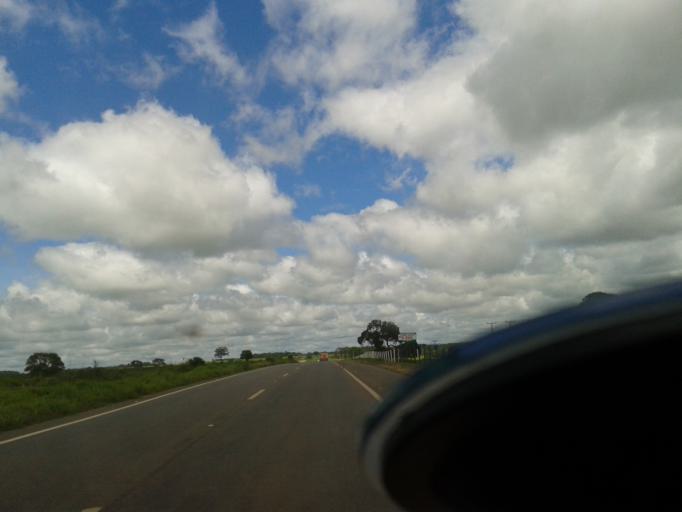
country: BR
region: Goias
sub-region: Itaberai
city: Itaberai
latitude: -16.1045
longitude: -49.6894
